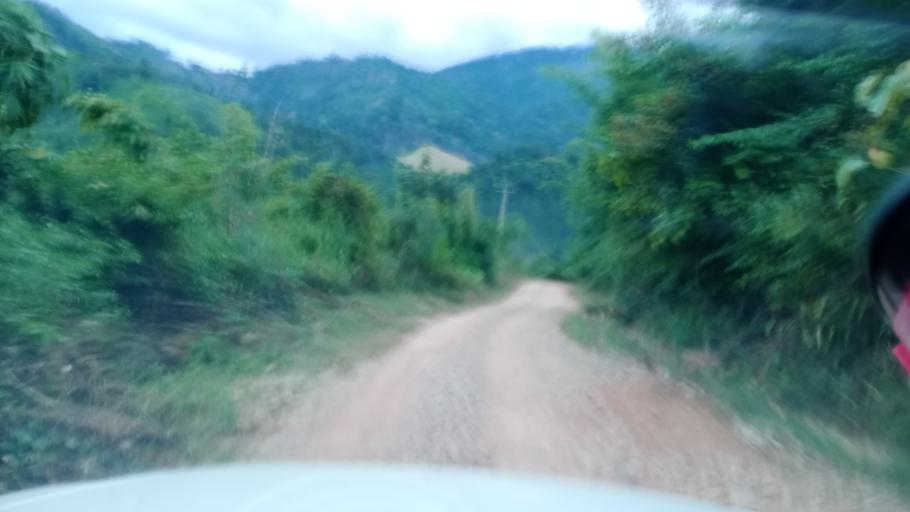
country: TH
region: Changwat Bueng Kan
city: Pak Khat
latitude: 18.7226
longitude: 103.2514
